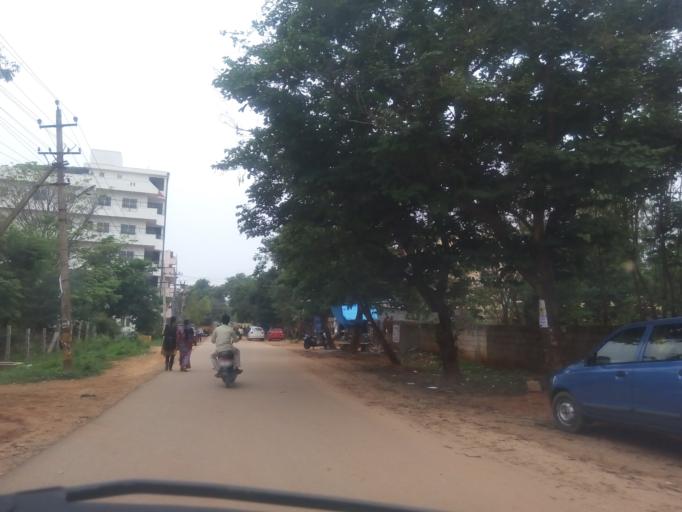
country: IN
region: Karnataka
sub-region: Bangalore Urban
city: Anekal
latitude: 12.8363
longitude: 77.6848
